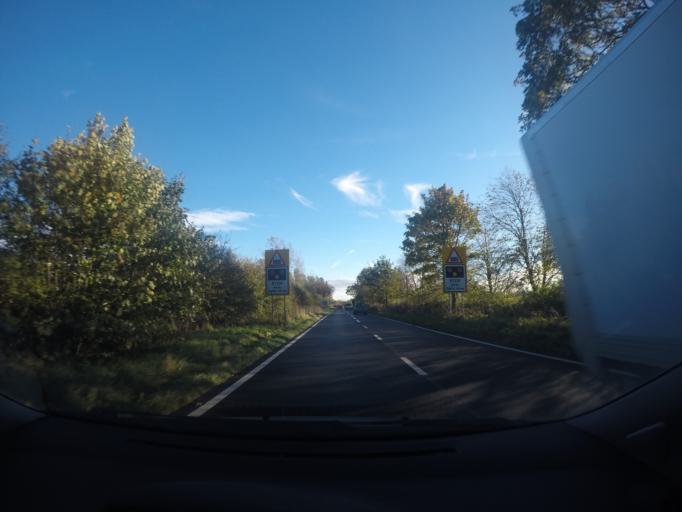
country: GB
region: England
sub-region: City of York
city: York
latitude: 53.9819
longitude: -1.0825
